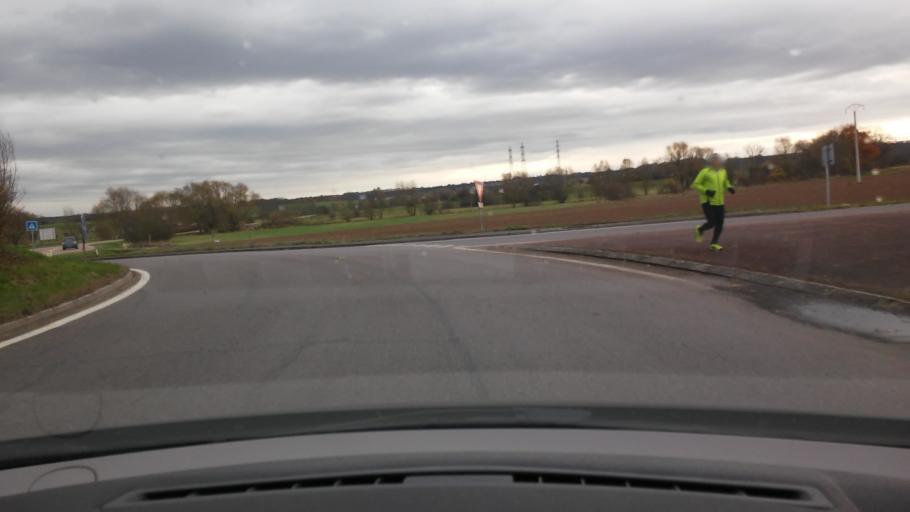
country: FR
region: Lorraine
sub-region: Departement de la Moselle
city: Argancy
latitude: 49.1703
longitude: 6.2143
